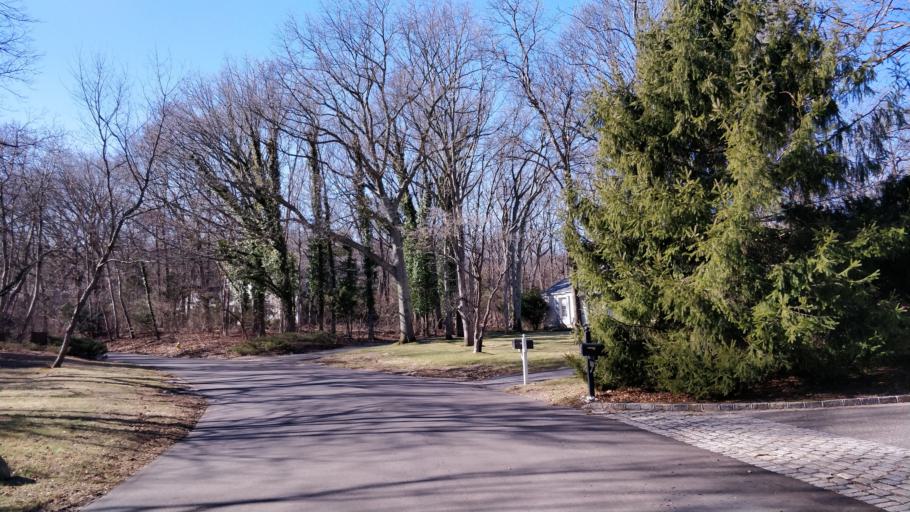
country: US
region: New York
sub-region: Suffolk County
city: Port Jefferson
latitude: 40.9673
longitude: -73.0658
